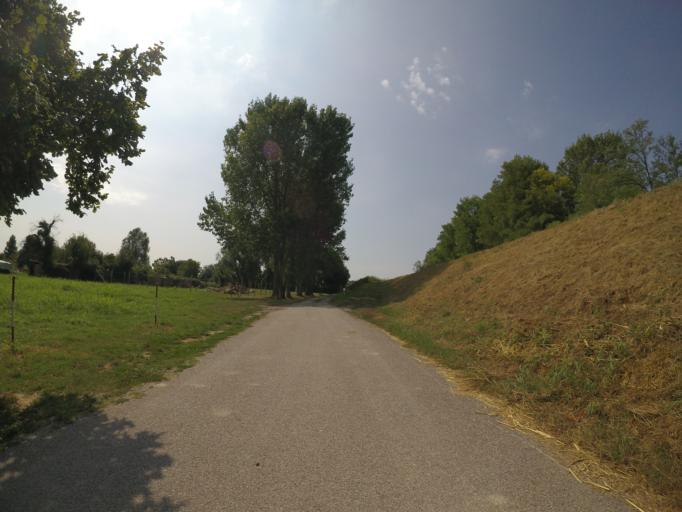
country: IT
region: Friuli Venezia Giulia
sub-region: Provincia di Udine
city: Pertegada
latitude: 45.7188
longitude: 13.0413
